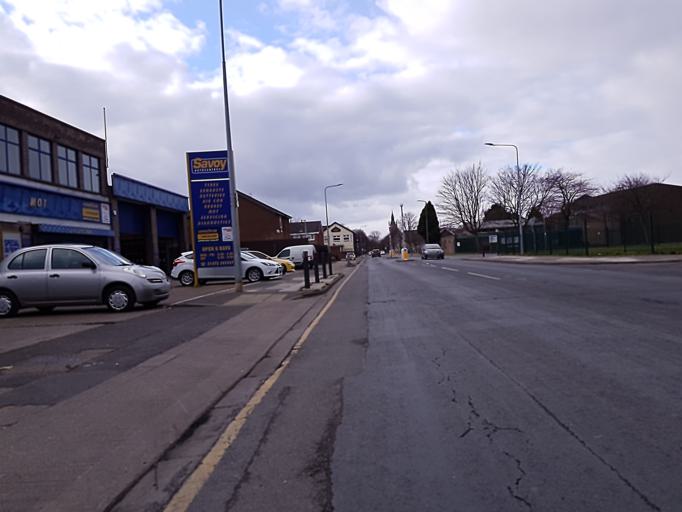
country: GB
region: England
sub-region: North East Lincolnshire
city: Grimsby
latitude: 53.5713
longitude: -0.0697
